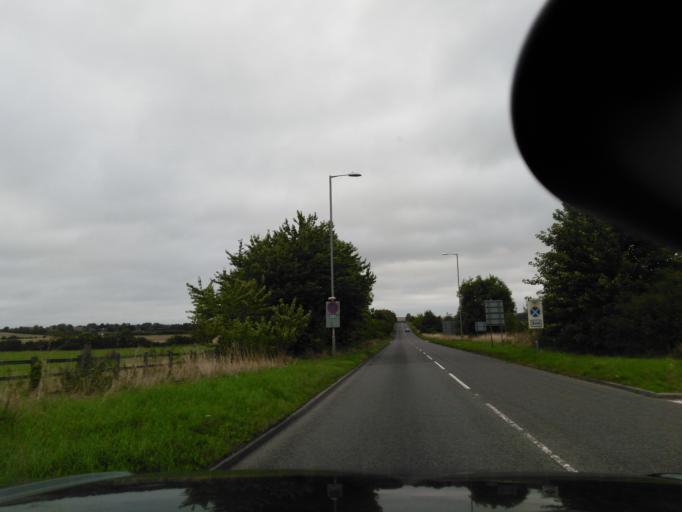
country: GB
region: England
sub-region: Wiltshire
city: Upton Scudamore
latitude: 51.2182
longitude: -2.2010
